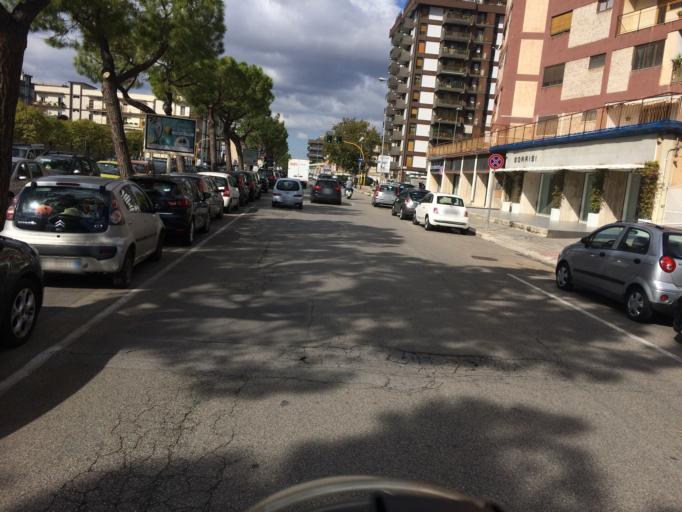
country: IT
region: Apulia
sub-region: Provincia di Bari
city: Bari
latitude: 41.1073
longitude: 16.8664
